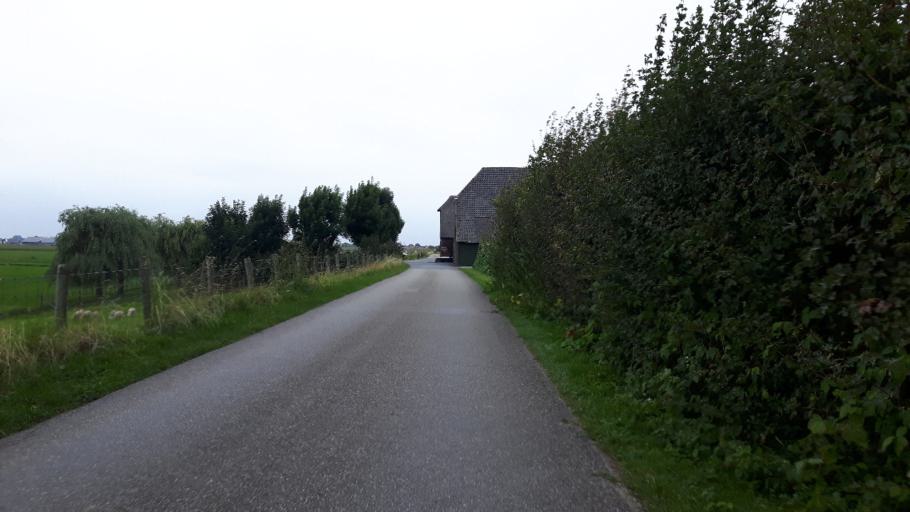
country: NL
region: South Holland
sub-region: Gemeente Kaag en Braassem
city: Leimuiden
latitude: 52.2206
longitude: 4.6910
